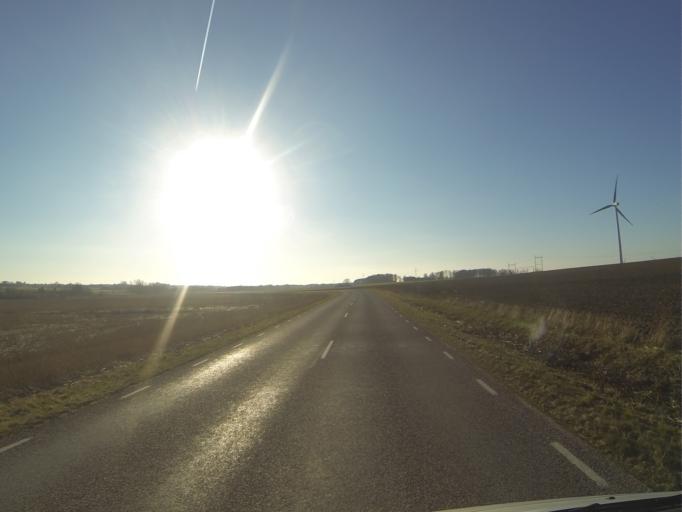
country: SE
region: Skane
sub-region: Hoors Kommun
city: Loberod
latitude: 55.7958
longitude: 13.5512
